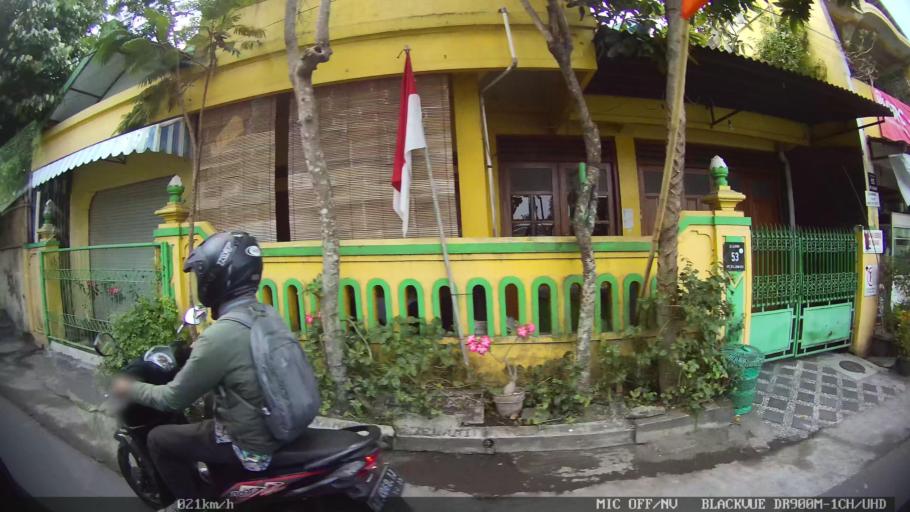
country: ID
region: Daerah Istimewa Yogyakarta
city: Yogyakarta
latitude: -7.8067
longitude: 110.3827
